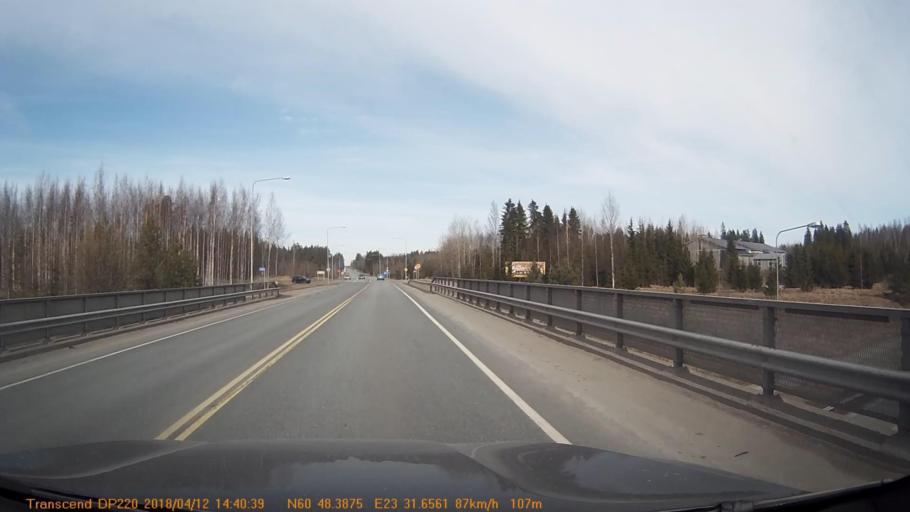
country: FI
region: Haeme
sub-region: Forssa
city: Jokioinen
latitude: 60.8077
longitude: 23.5298
